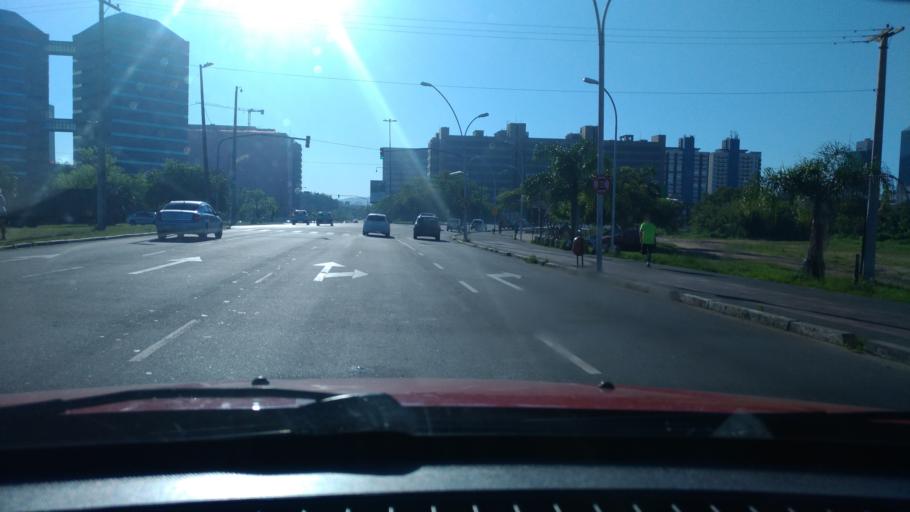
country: BR
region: Rio Grande do Sul
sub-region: Porto Alegre
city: Porto Alegre
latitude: -30.0427
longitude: -51.2342
